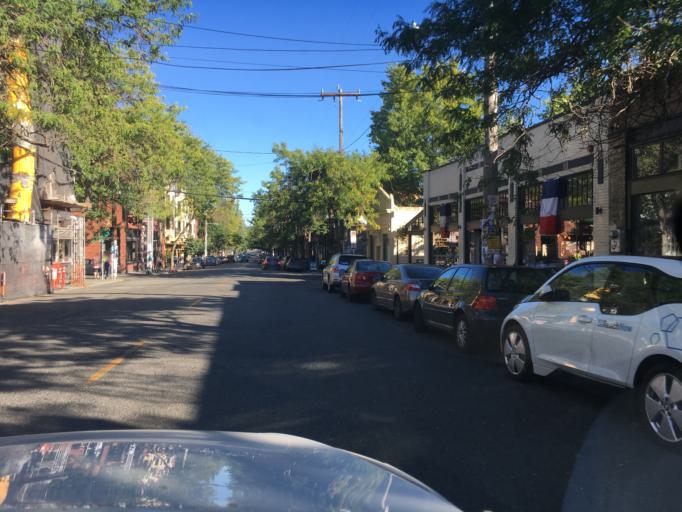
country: US
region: Washington
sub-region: King County
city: Seattle
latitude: 47.6668
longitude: -122.3837
